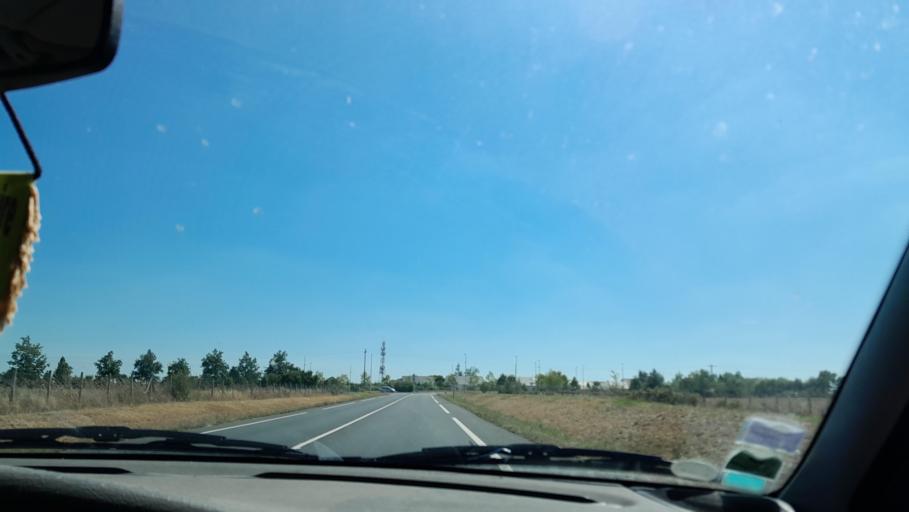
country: FR
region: Pays de la Loire
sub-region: Departement de la Loire-Atlantique
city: Saint-Gereon
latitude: 47.3708
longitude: -1.2124
